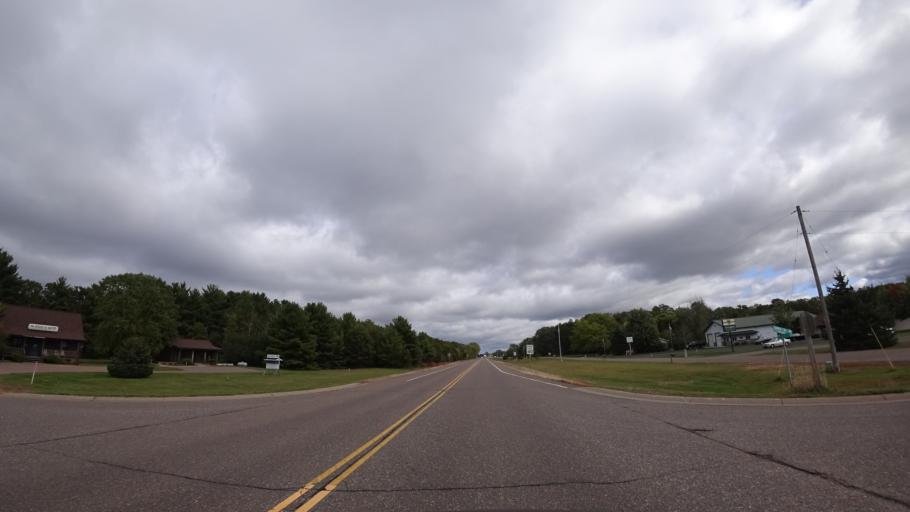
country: US
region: Wisconsin
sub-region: Chippewa County
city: Lake Wissota
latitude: 44.9224
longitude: -91.3297
